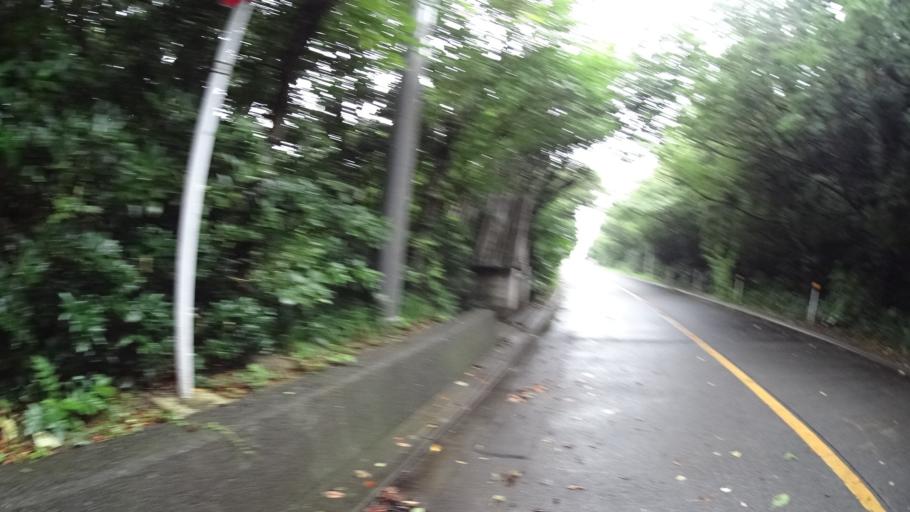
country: JP
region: Shizuoka
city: Shimoda
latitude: 34.3332
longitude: 139.2126
